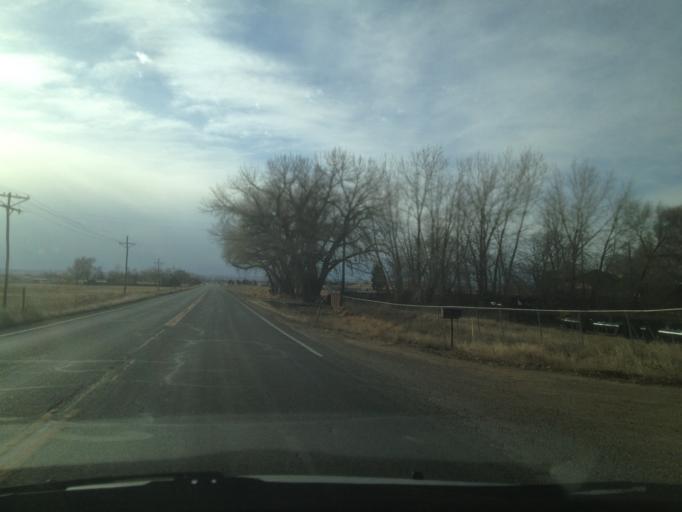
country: US
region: Colorado
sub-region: Weld County
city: Aristocrat Ranchettes
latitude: 40.0803
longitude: -104.7640
